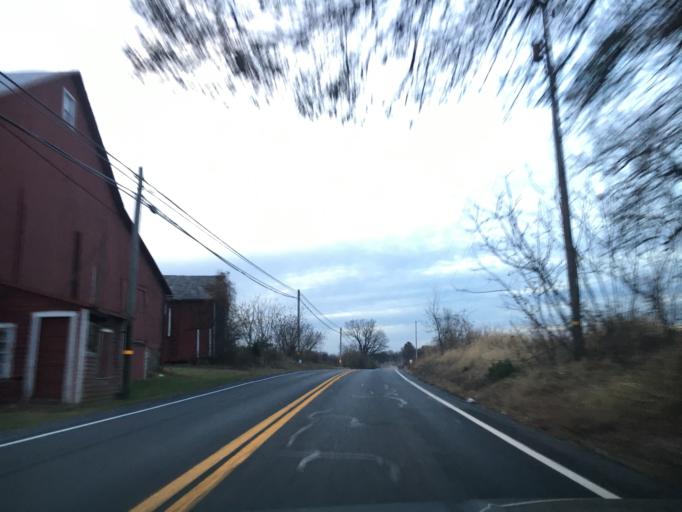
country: US
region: Pennsylvania
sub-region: Lehigh County
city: Stiles
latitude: 40.6450
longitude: -75.5250
